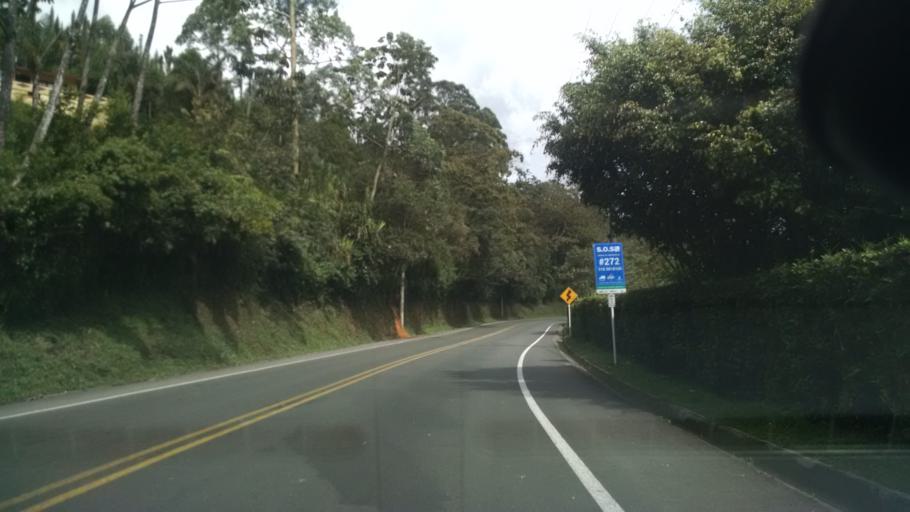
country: CO
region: Antioquia
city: Caldas
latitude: 6.0386
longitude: -75.6275
